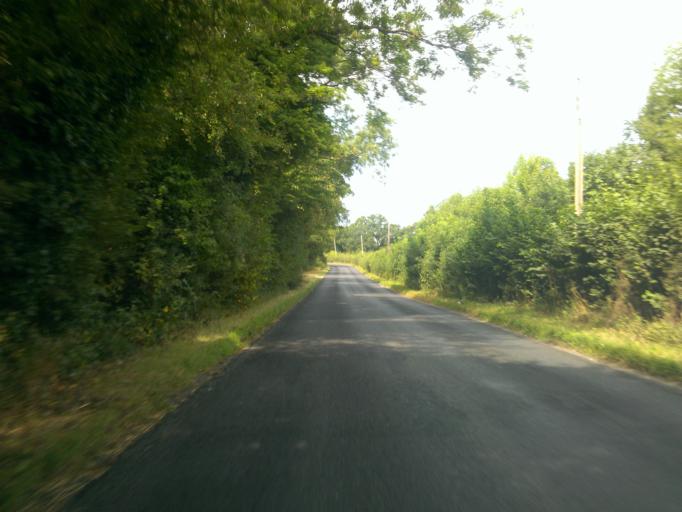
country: GB
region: England
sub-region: Kent
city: Sevenoaks
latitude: 51.2013
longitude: 0.1518
